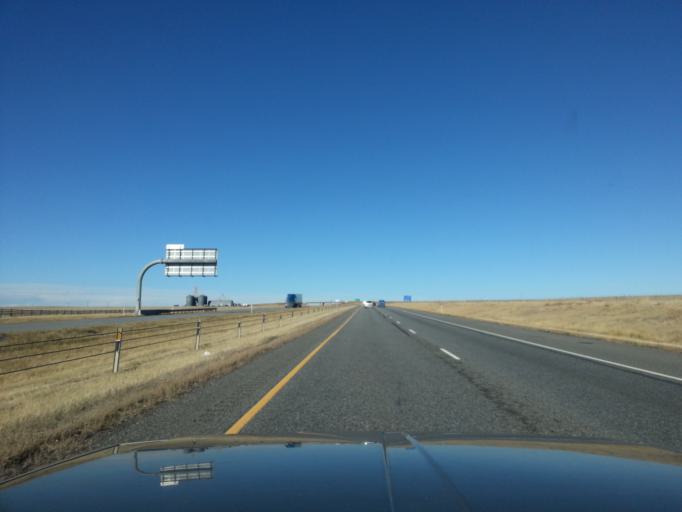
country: US
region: Colorado
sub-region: Adams County
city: Aurora
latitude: 39.8468
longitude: -104.7467
